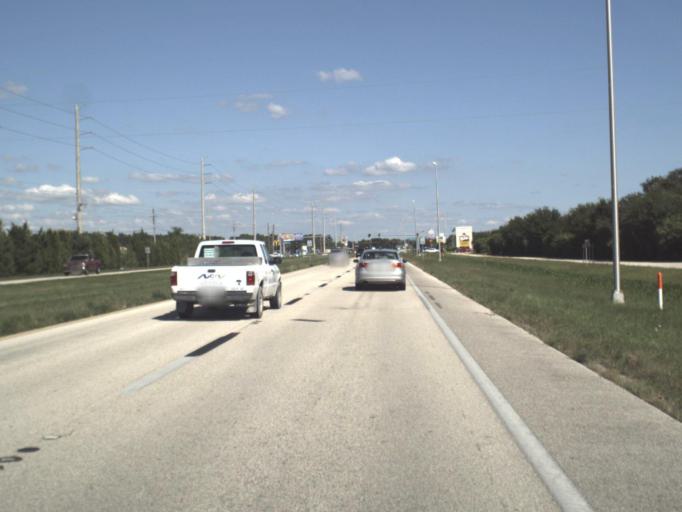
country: US
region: Florida
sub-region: Charlotte County
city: Rotonda
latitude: 26.9330
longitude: -82.2300
